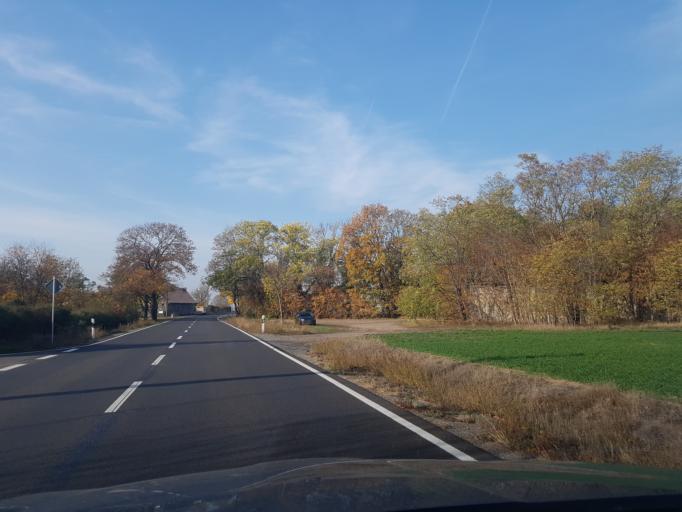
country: DE
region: Saxony
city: Arzberg
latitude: 51.5432
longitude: 13.1717
